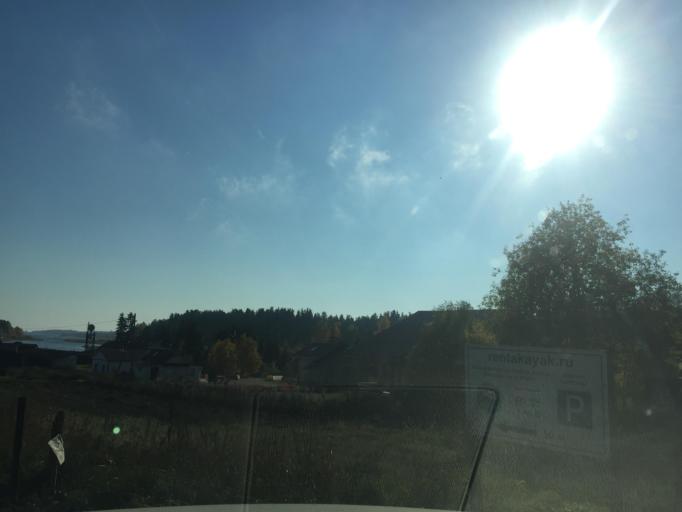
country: RU
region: Leningrad
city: Kuznechnoye
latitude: 61.2941
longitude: 30.0580
